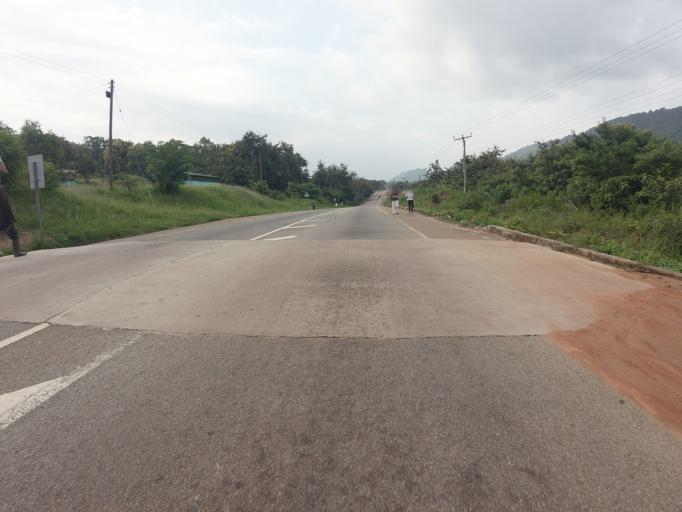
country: GH
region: Volta
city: Ho
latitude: 6.6616
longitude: 0.4722
